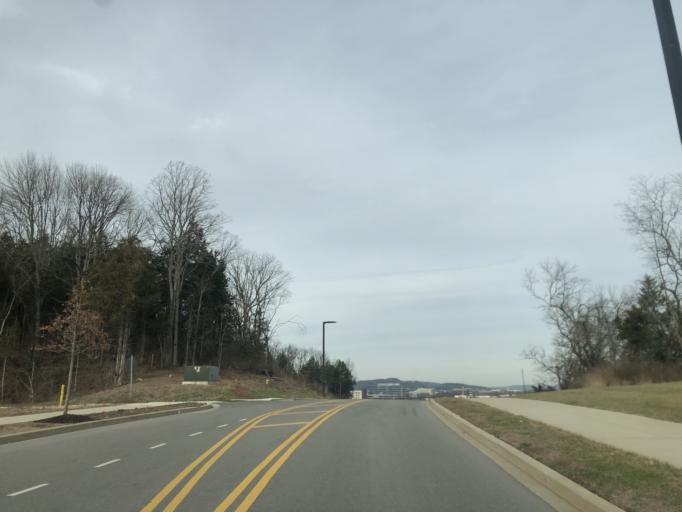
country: US
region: Tennessee
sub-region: Williamson County
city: Franklin
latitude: 35.9259
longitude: -86.8110
